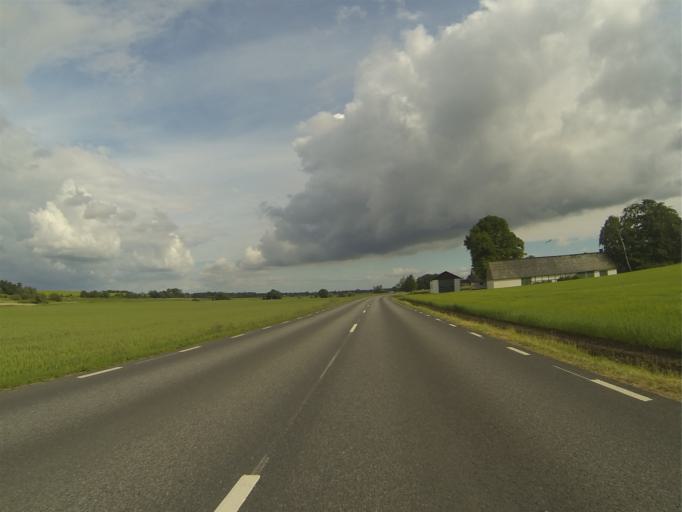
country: SE
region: Skane
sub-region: Eslovs Kommun
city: Eslov
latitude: 55.7590
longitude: 13.3174
